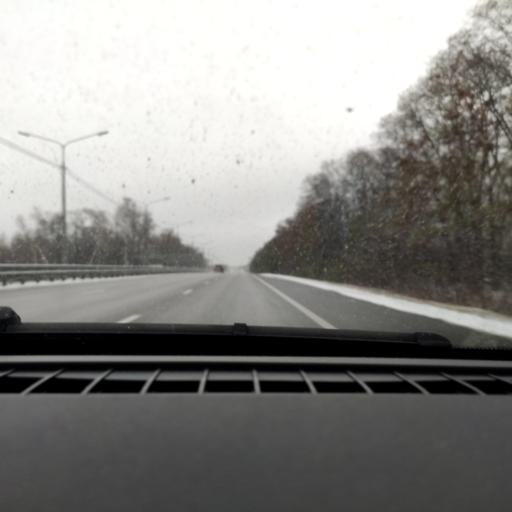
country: RU
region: Voronezj
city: Podgornoye
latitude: 51.8166
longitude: 39.2083
